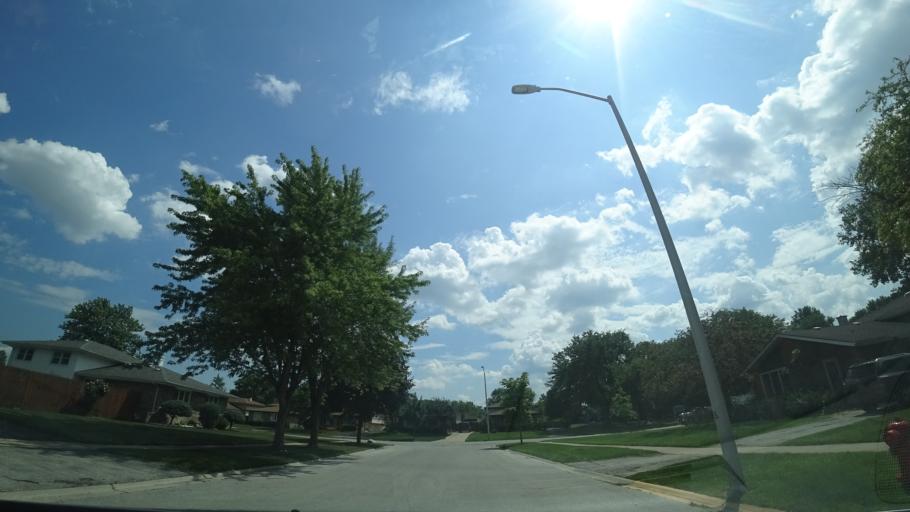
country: US
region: Illinois
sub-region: Cook County
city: Alsip
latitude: 41.6730
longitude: -87.7263
